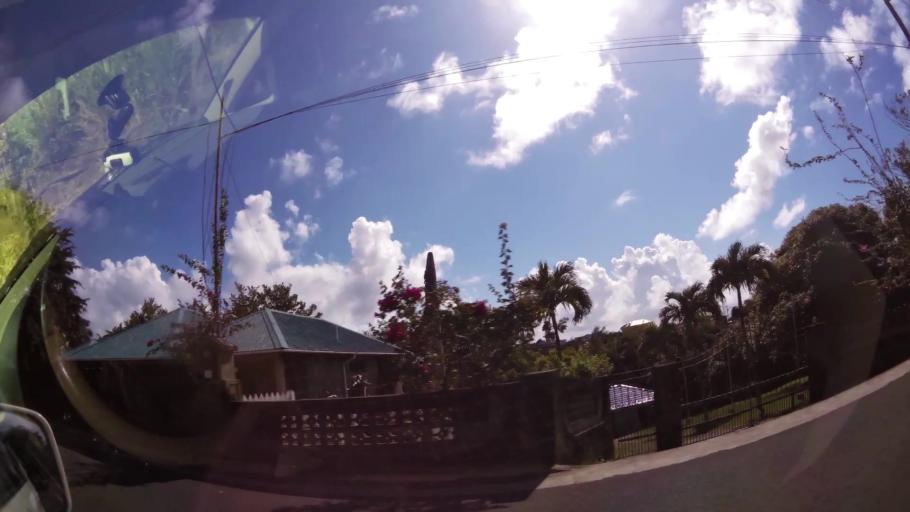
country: VC
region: Saint George
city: Kingstown
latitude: 13.1343
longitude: -61.1814
